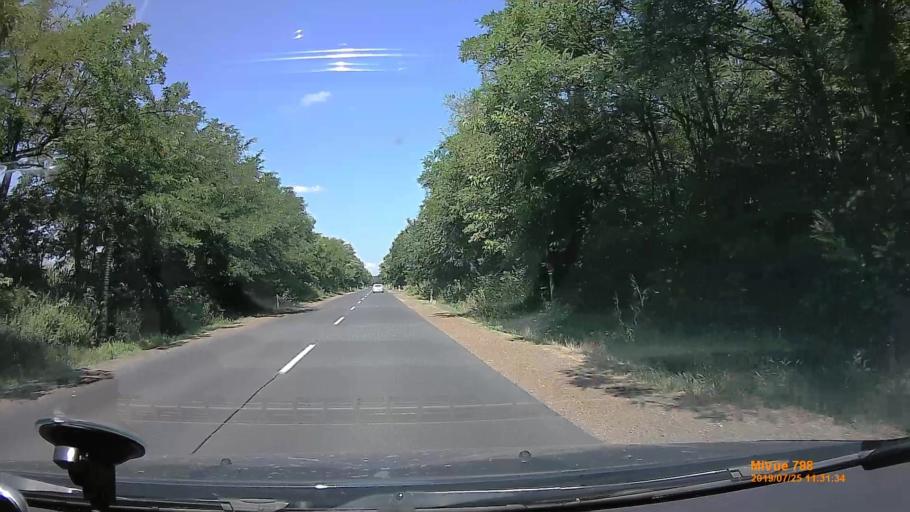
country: HU
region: Szabolcs-Szatmar-Bereg
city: Nagykallo
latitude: 47.9080
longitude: 21.7821
